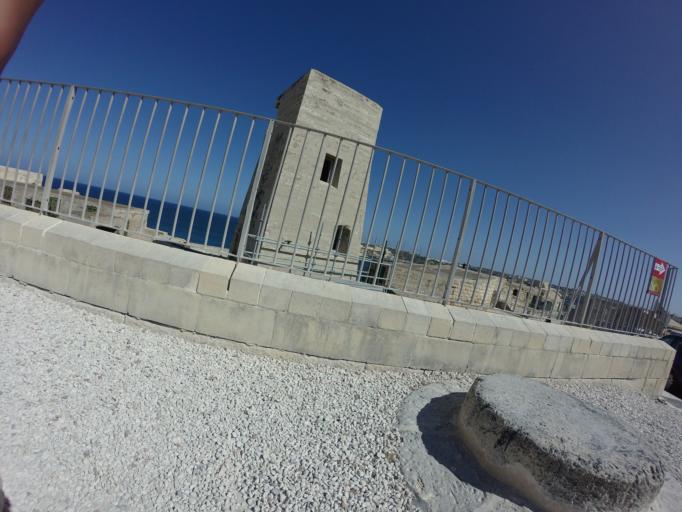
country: MT
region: Il-Belt Valletta
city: Valletta
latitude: 35.9008
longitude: 14.5187
